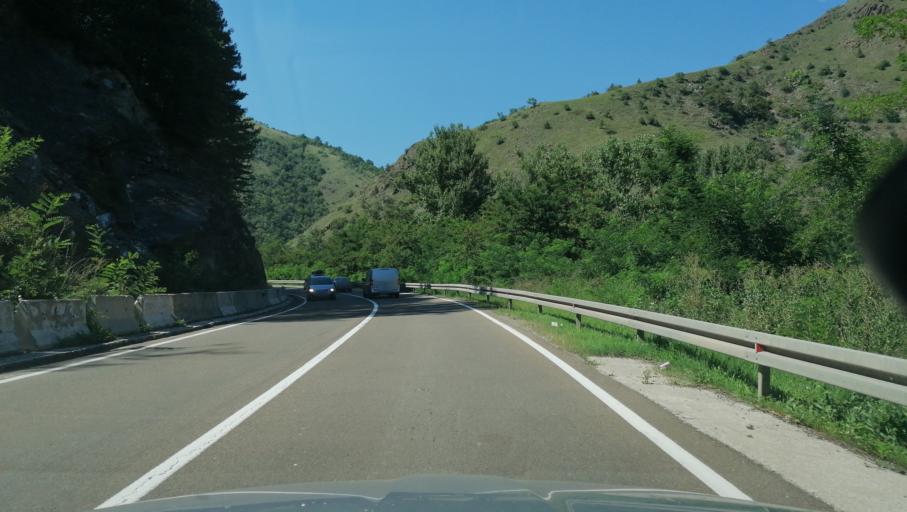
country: RS
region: Central Serbia
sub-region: Raski Okrug
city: Kraljevo
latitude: 43.5815
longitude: 20.5843
